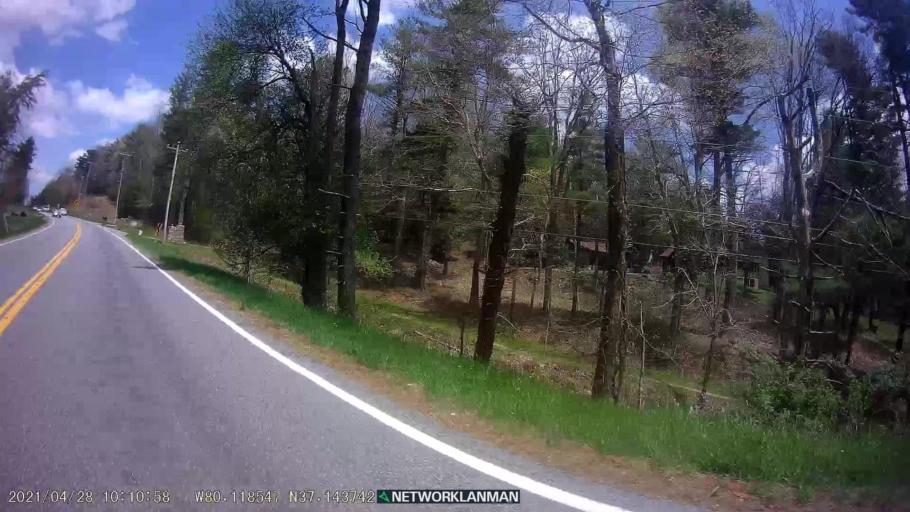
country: US
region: Virginia
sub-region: Roanoke County
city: Cave Spring
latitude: 37.1441
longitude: -80.1186
